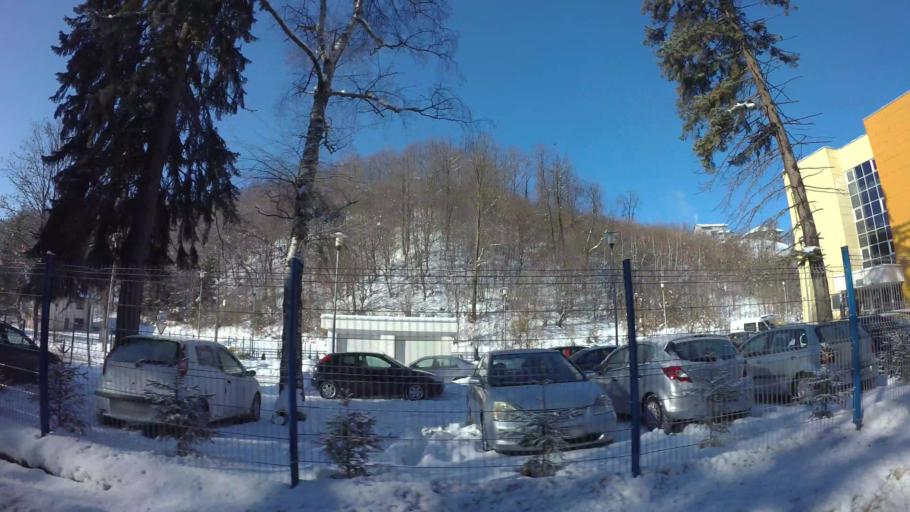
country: BA
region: Federation of Bosnia and Herzegovina
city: Kobilja Glava
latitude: 43.8877
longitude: 18.4162
